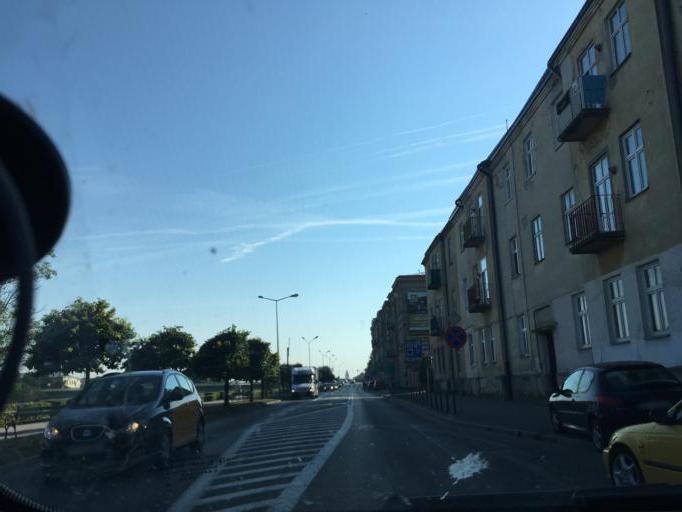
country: PL
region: Subcarpathian Voivodeship
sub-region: Przemysl
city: Przemysl
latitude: 49.7828
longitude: 22.7645
